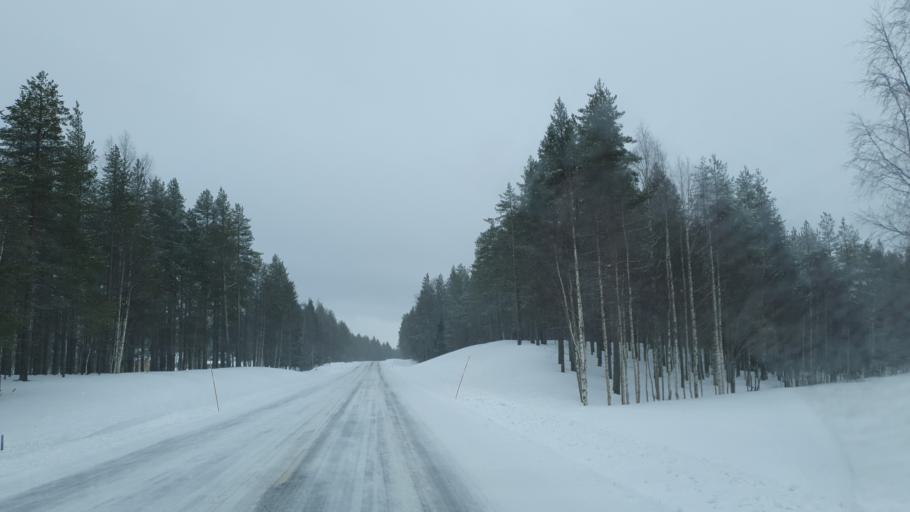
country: FI
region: Lapland
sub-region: Rovaniemi
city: Ranua
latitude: 66.1749
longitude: 26.2312
